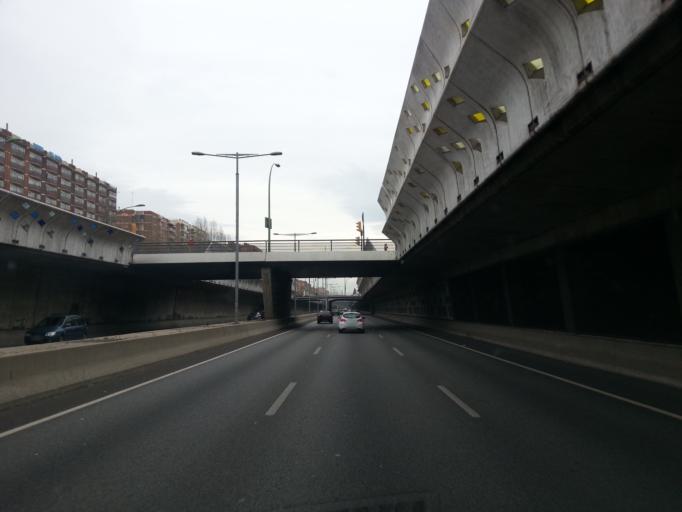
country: ES
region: Catalonia
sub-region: Provincia de Barcelona
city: Sant Marti
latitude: 41.4108
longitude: 2.1968
